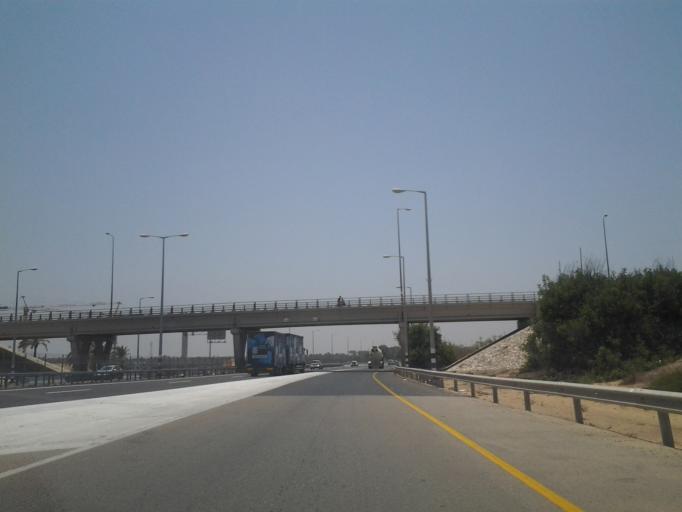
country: IL
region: Haifa
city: Hadera
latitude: 32.4446
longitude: 34.8925
